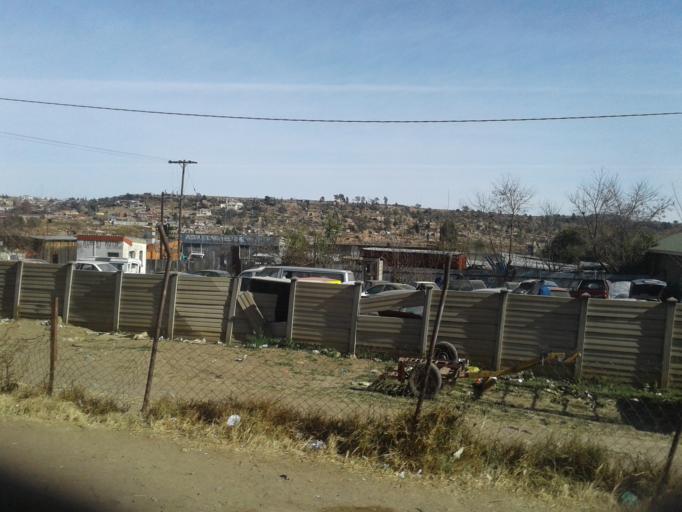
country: LS
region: Maseru
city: Maseru
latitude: -29.3048
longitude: 27.5155
